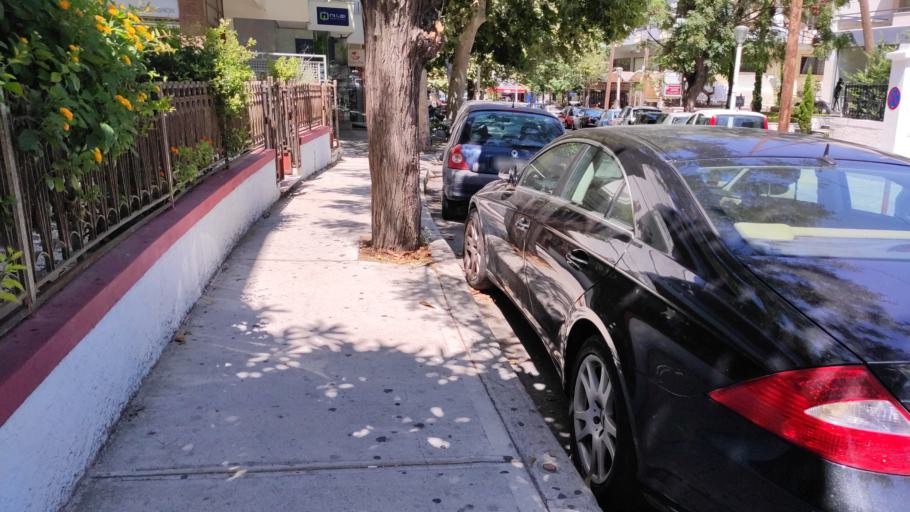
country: GR
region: South Aegean
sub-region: Nomos Dodekanisou
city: Rodos
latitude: 36.4504
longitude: 28.2215
